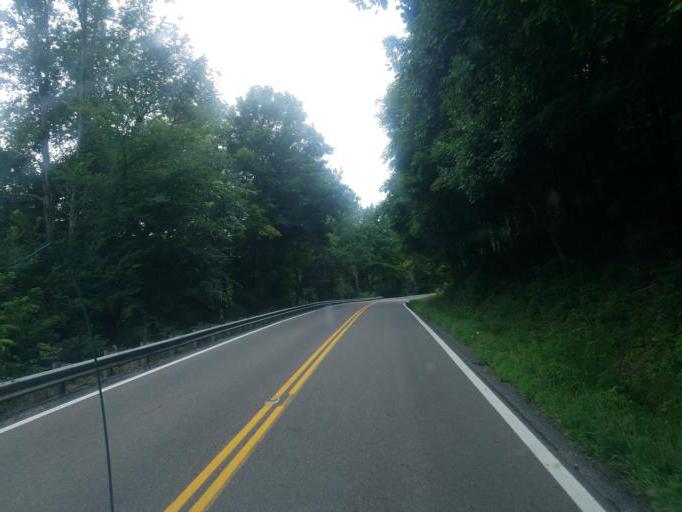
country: US
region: Ohio
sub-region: Knox County
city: Oak Hill
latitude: 40.3527
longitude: -82.1382
